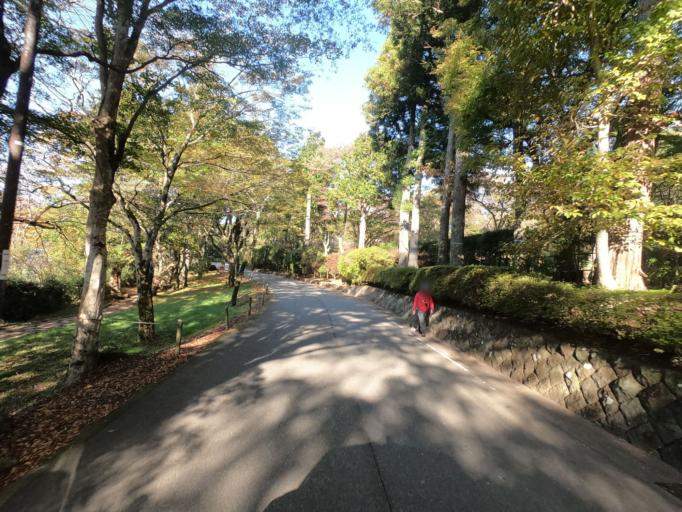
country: JP
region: Kanagawa
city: Hakone
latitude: 35.2045
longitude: 139.0205
